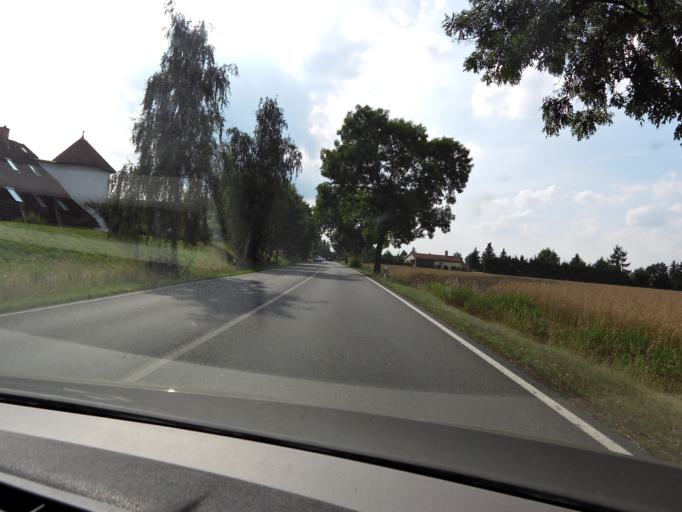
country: DE
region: Saxony
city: Grossposna
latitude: 51.2625
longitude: 12.5096
